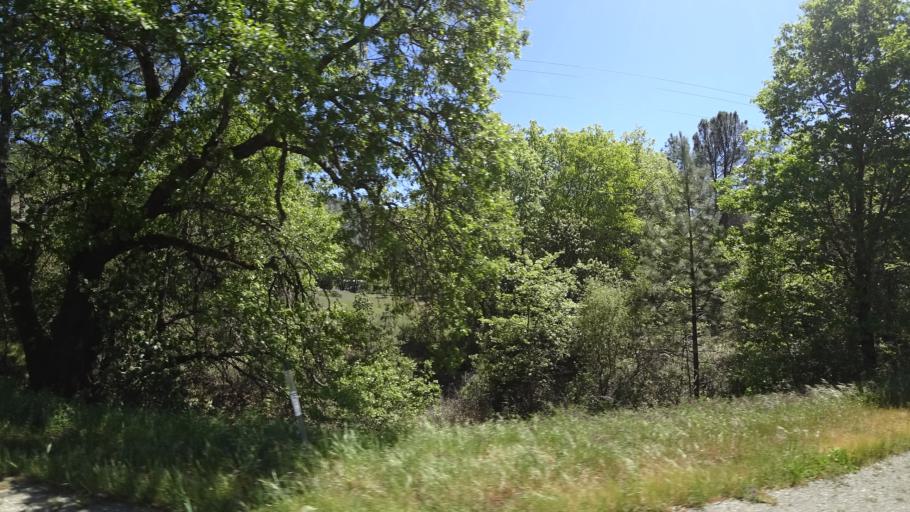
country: US
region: California
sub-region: Trinity County
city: Weaverville
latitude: 40.7278
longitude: -123.0410
